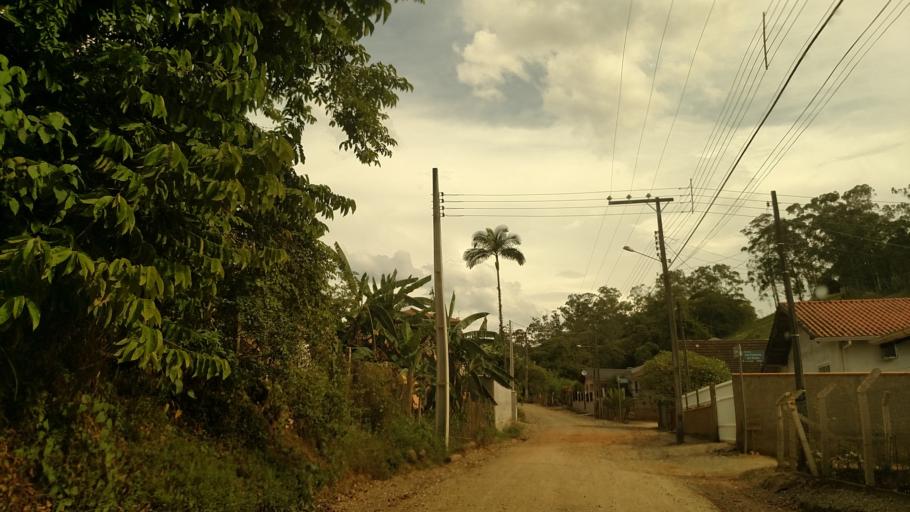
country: BR
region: Santa Catarina
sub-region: Brusque
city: Brusque
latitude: -27.0390
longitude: -48.8575
